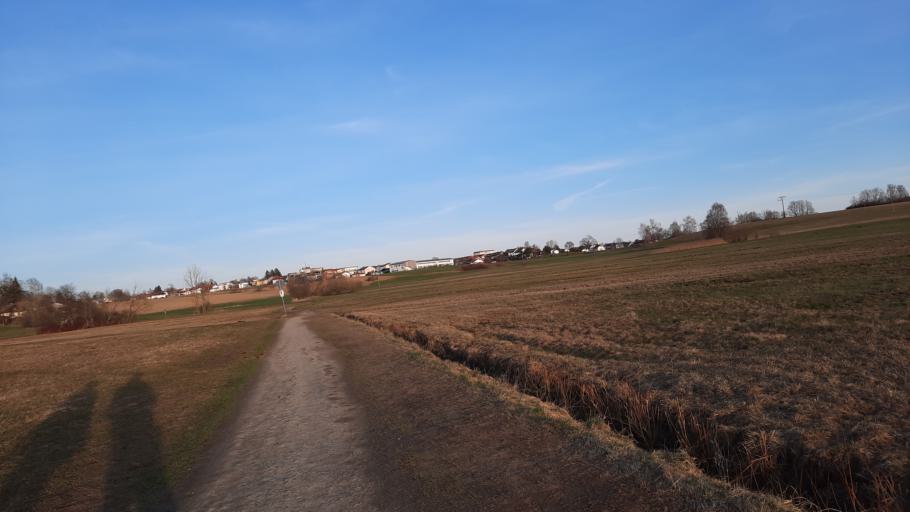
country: DE
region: Bavaria
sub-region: Upper Bavaria
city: Ebersberg
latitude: 48.0782
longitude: 11.9438
